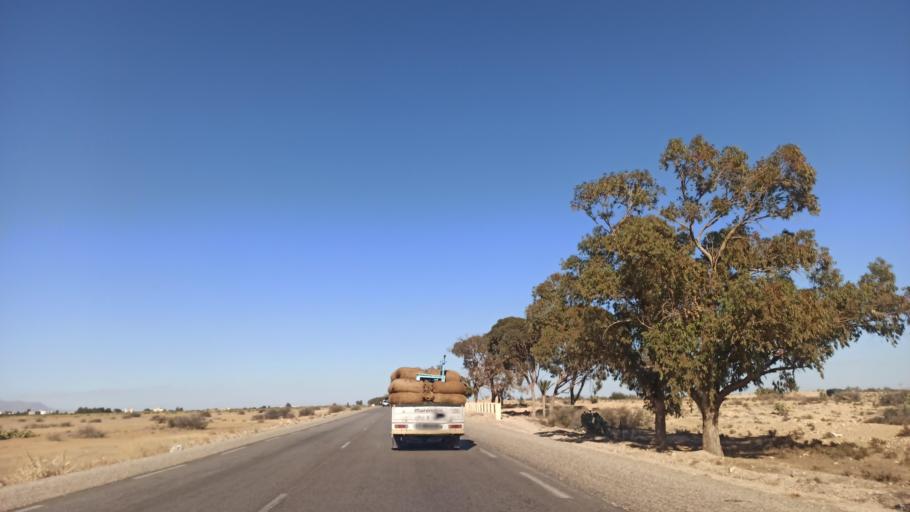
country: TN
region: Sidi Bu Zayd
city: Jilma
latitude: 35.2039
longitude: 9.3784
